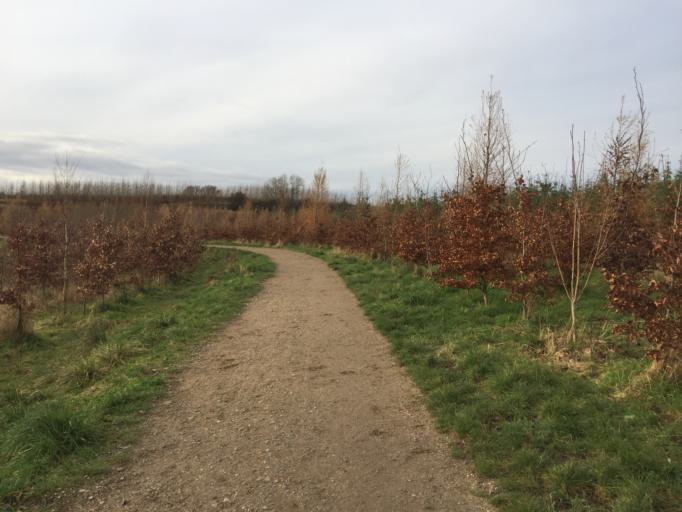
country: DK
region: South Denmark
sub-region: Odense Kommune
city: Bellinge
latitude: 55.3712
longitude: 10.3141
